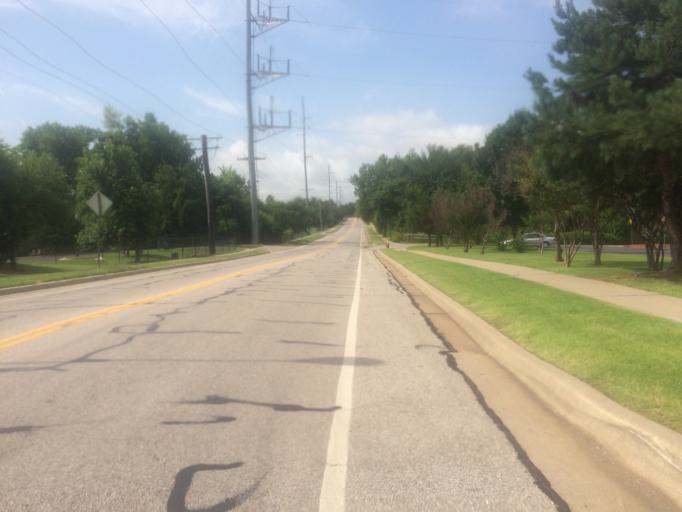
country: US
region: Oklahoma
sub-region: Cleveland County
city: Norman
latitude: 35.1867
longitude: -97.4236
